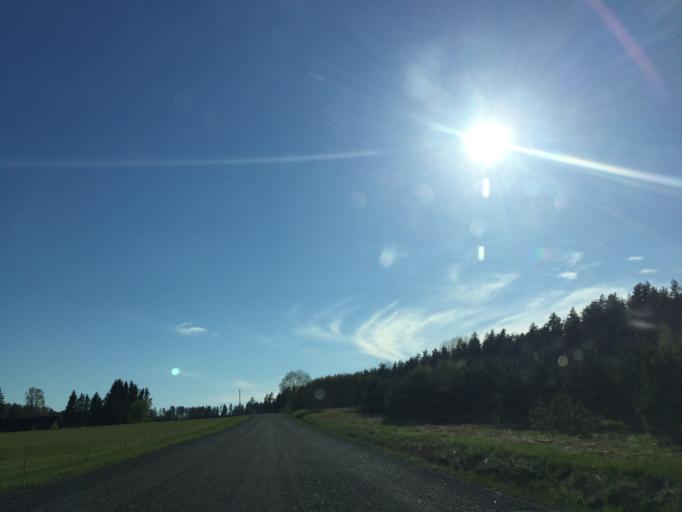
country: EE
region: Valgamaa
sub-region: Valga linn
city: Valga
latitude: 57.8270
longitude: 26.2156
